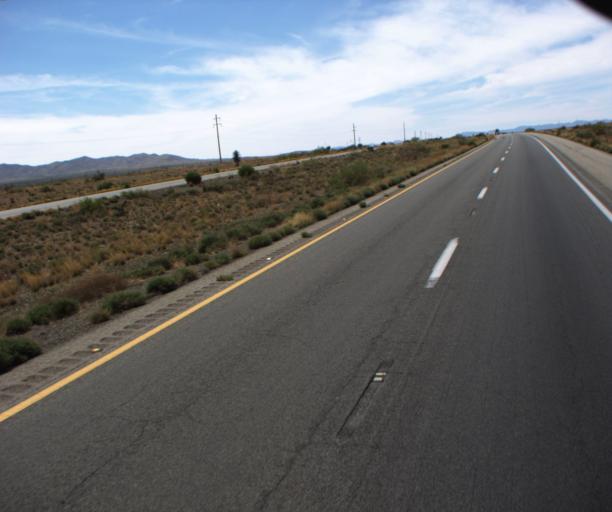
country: US
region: Arizona
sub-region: Cochise County
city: Willcox
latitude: 32.3627
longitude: -109.6456
